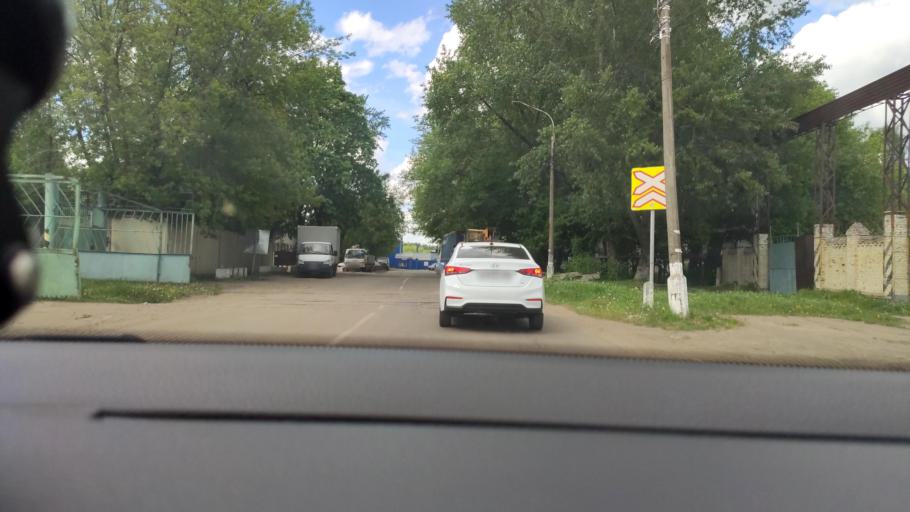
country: RU
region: Moskovskaya
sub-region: Podol'skiy Rayon
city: Podol'sk
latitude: 55.4426
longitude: 37.5737
